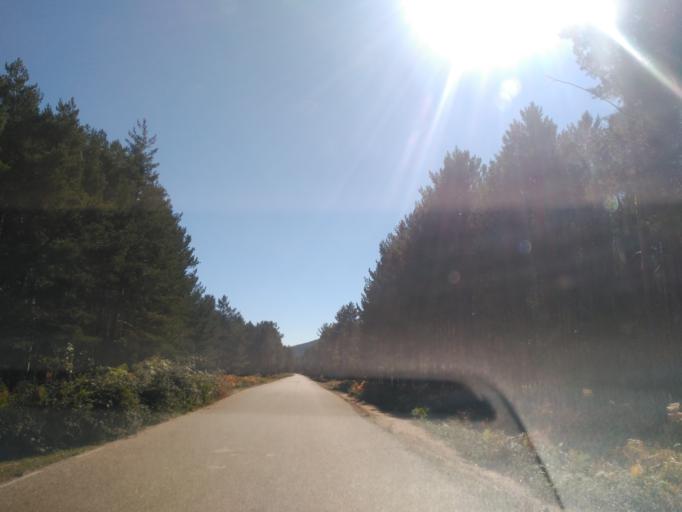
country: ES
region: Castille and Leon
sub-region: Provincia de Soria
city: Vinuesa
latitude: 41.9487
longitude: -2.7810
